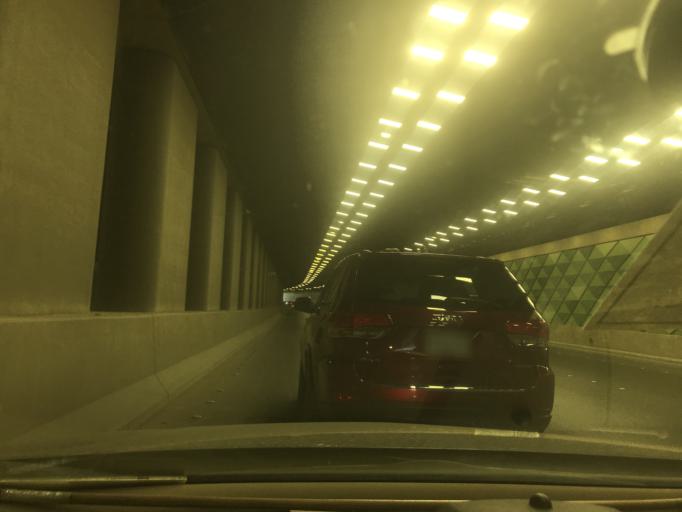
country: SA
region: Ar Riyad
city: Riyadh
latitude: 24.6943
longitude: 46.7232
